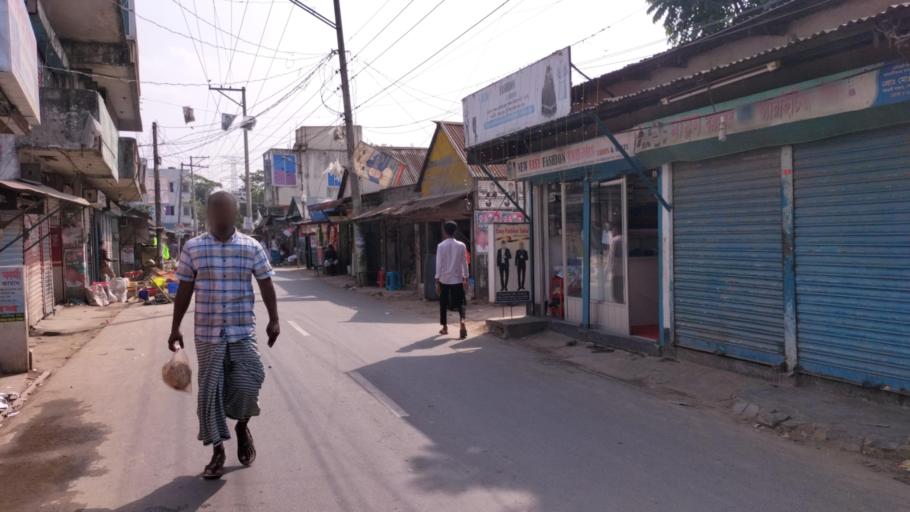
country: BD
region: Dhaka
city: Azimpur
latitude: 23.7560
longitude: 90.2929
